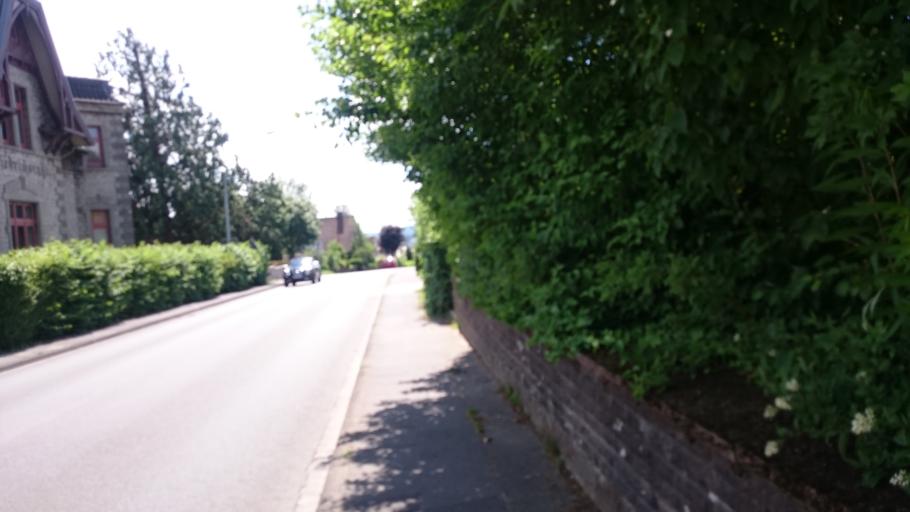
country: DE
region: North Rhine-Westphalia
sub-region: Regierungsbezirk Detmold
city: Lage
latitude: 52.0013
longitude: 8.7968
